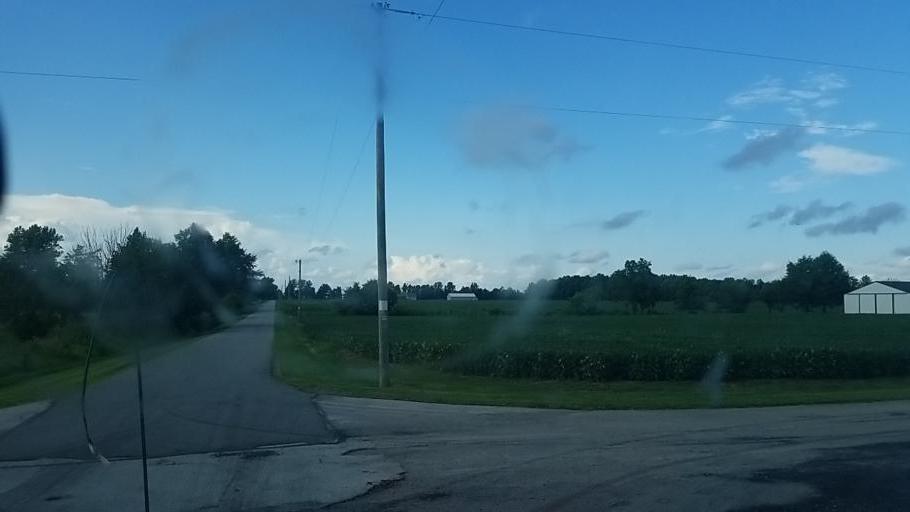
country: US
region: Ohio
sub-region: Hardin County
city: Forest
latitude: 40.7888
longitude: -83.4484
